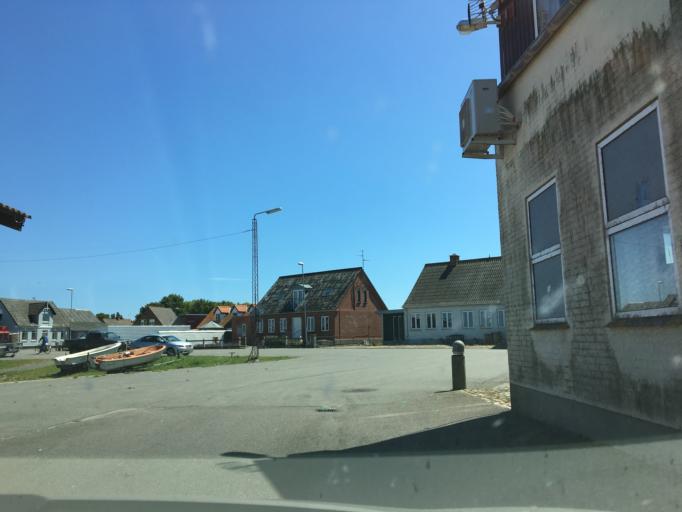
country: DK
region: South Denmark
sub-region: AEro Kommune
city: Marstal
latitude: 54.7506
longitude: 10.6707
